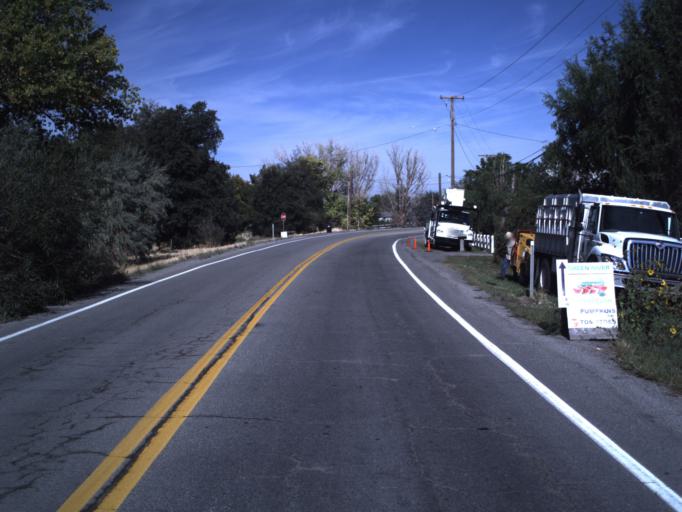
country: US
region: Utah
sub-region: Utah County
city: Orem
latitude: 40.2585
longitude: -111.7140
